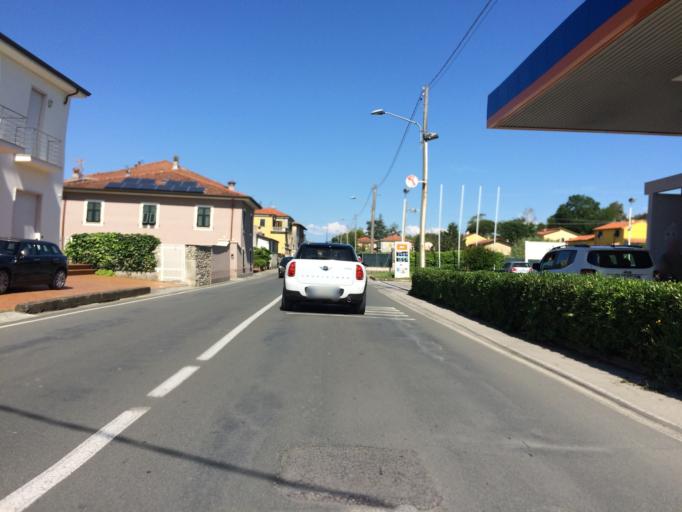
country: IT
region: Liguria
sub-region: Provincia di La Spezia
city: Sarzana
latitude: 44.1060
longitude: 9.9733
